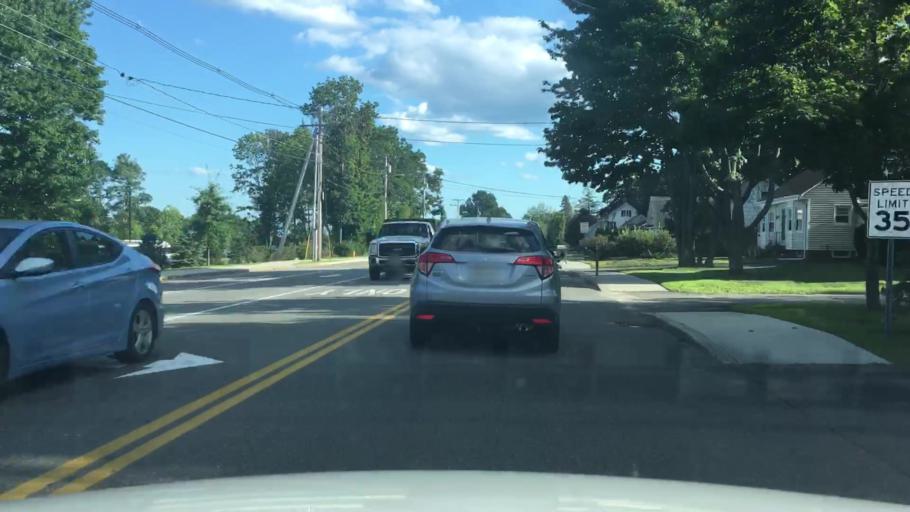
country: US
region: Maine
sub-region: Cumberland County
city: Scarborough
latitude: 43.5897
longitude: -70.3344
